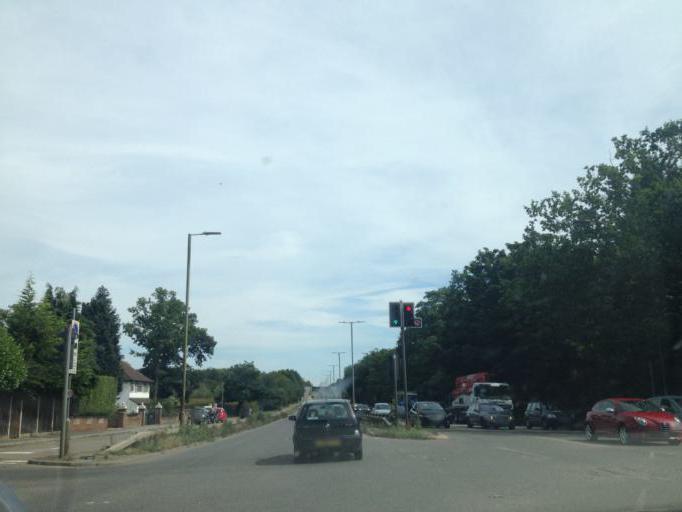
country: GB
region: England
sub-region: Hertfordshire
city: Watford
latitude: 51.6763
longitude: -0.3789
